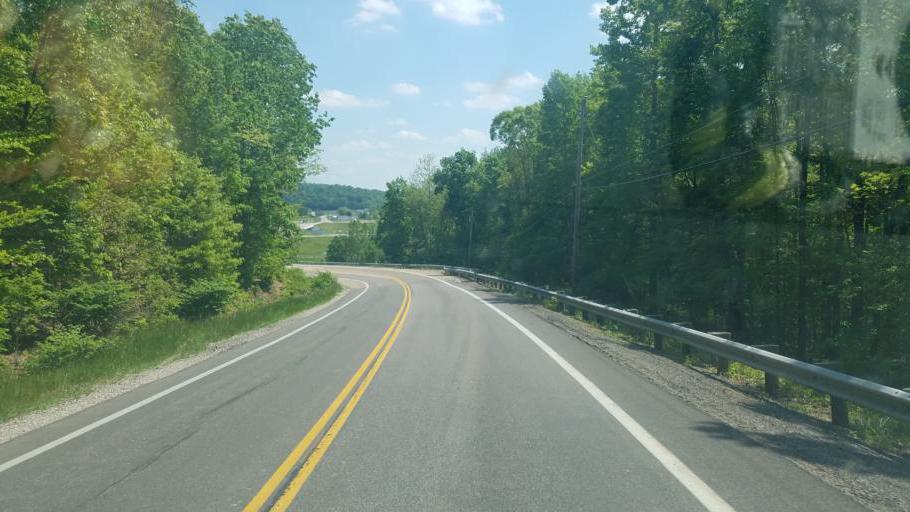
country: US
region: Ohio
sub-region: Muskingum County
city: Frazeysburg
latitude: 40.1075
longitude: -82.1800
